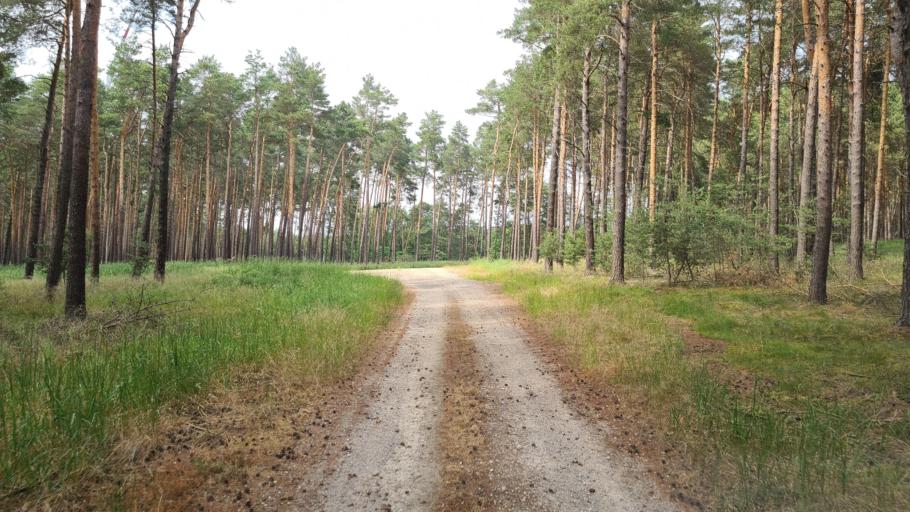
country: DE
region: Brandenburg
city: Schilda
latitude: 51.6599
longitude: 13.3519
